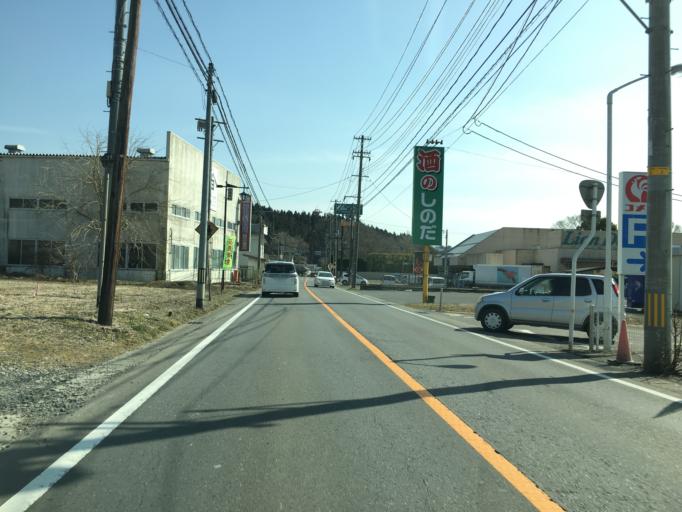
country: JP
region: Ibaraki
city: Daigo
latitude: 36.8789
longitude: 140.4221
